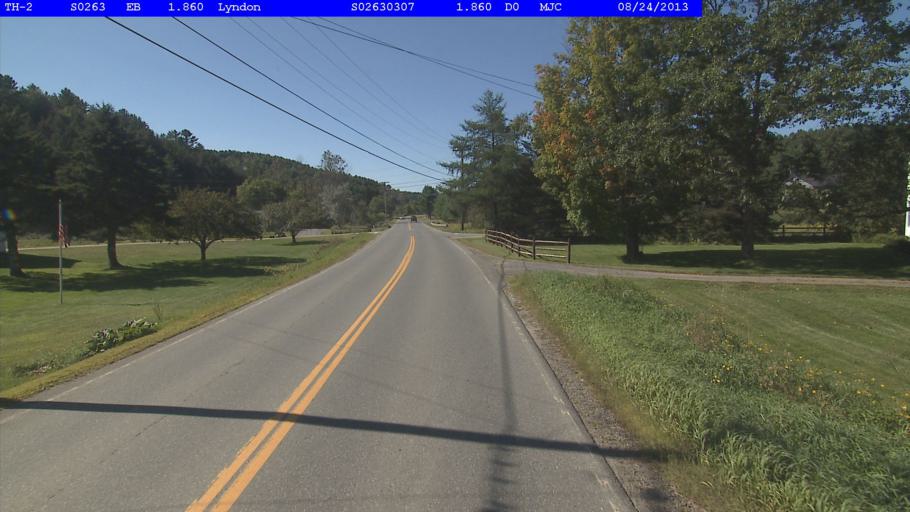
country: US
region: Vermont
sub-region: Caledonia County
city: Lyndon
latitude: 44.5112
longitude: -71.9934
